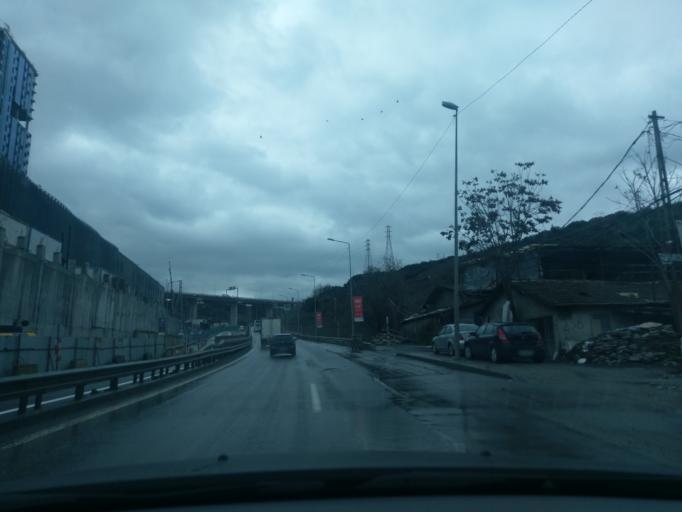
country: TR
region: Istanbul
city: Sisli
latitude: 41.0913
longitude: 28.9538
